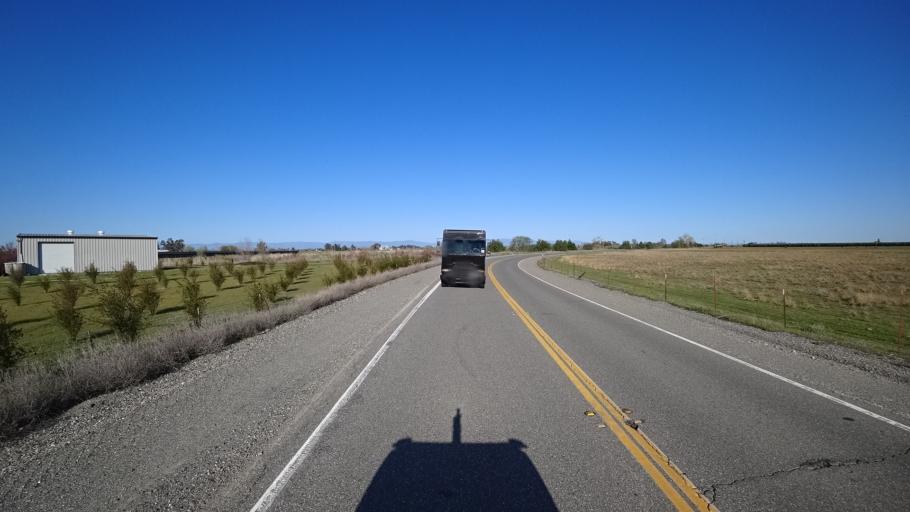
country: US
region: California
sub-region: Glenn County
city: Hamilton City
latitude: 39.7463
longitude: -122.0965
